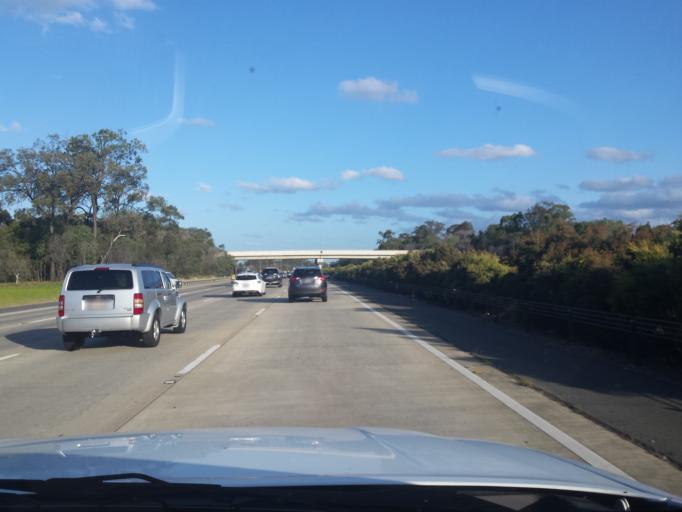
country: AU
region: Queensland
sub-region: Gold Coast
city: Ormeau Hills
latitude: -27.7571
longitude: 153.2409
